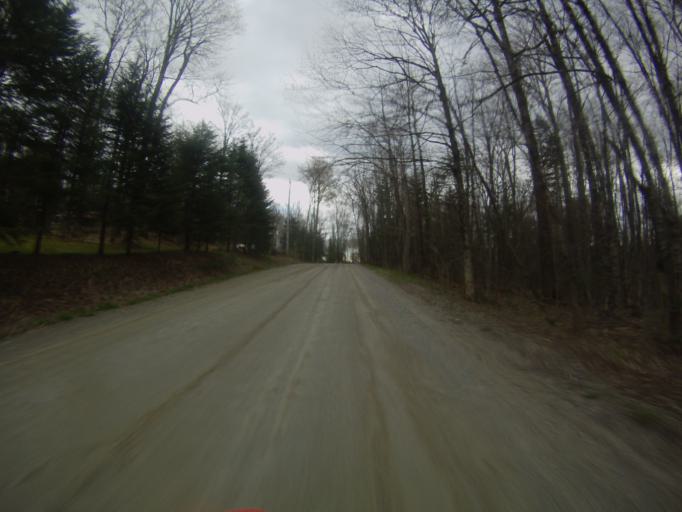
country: US
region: Vermont
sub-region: Addison County
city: Bristol
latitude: 44.0563
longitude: -73.0094
